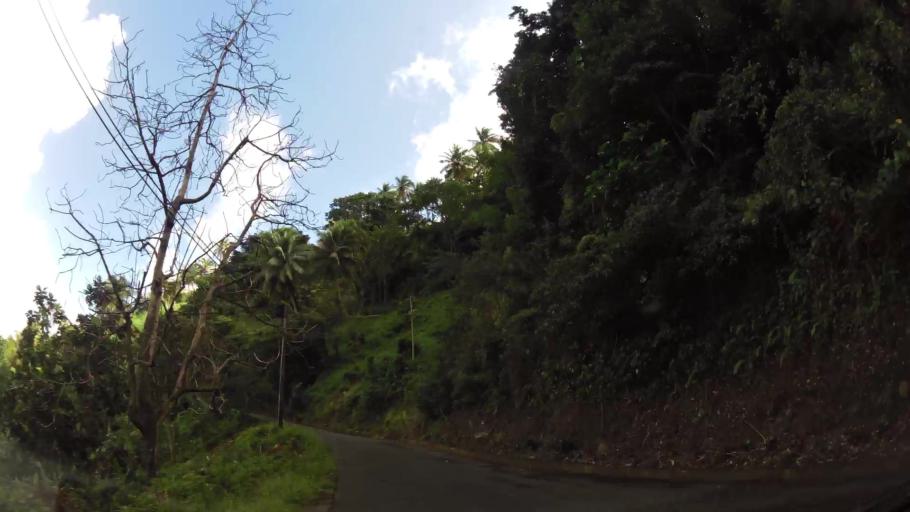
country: DM
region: Saint John
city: Portsmouth
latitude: 15.6180
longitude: -61.4163
